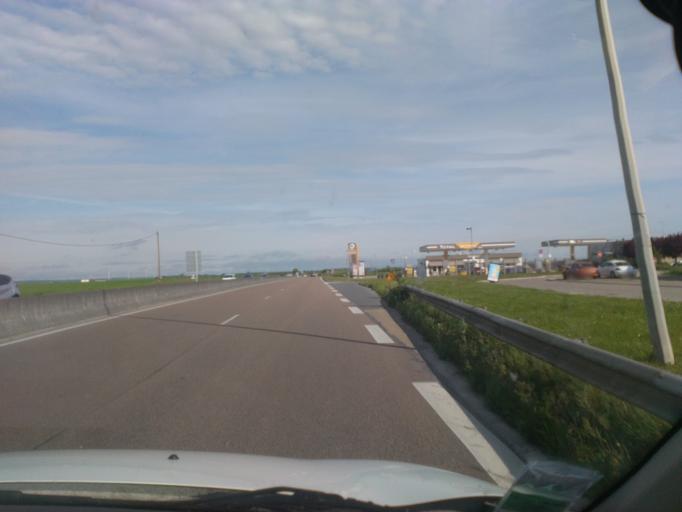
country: FR
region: Champagne-Ardenne
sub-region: Departement de l'Aube
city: La Chapelle-Saint-Luc
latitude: 48.3350
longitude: 4.0192
